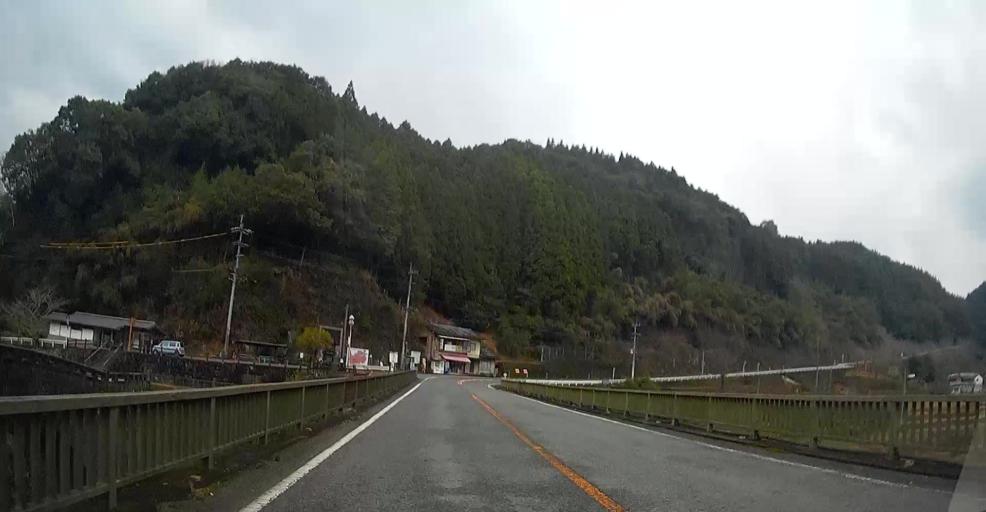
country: JP
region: Kumamoto
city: Matsubase
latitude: 32.6292
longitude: 130.8885
